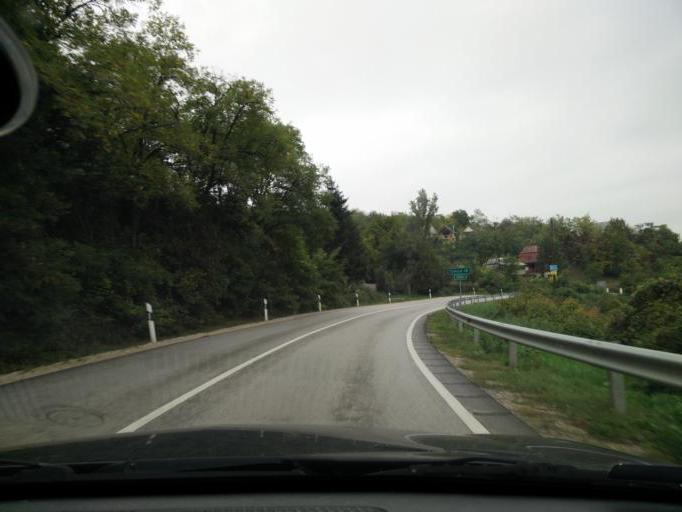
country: HU
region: Komarom-Esztergom
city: Tokod
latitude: 47.7140
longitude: 18.6263
